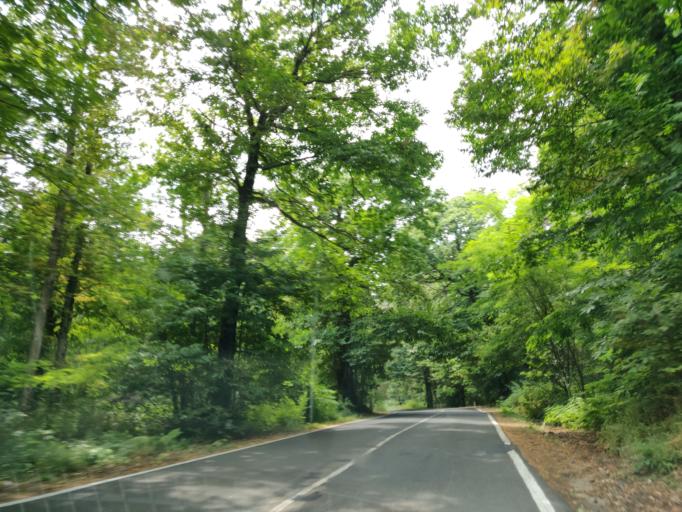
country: IT
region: Tuscany
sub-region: Provincia di Siena
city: Abbadia San Salvatore
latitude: 42.8890
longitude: 11.6577
